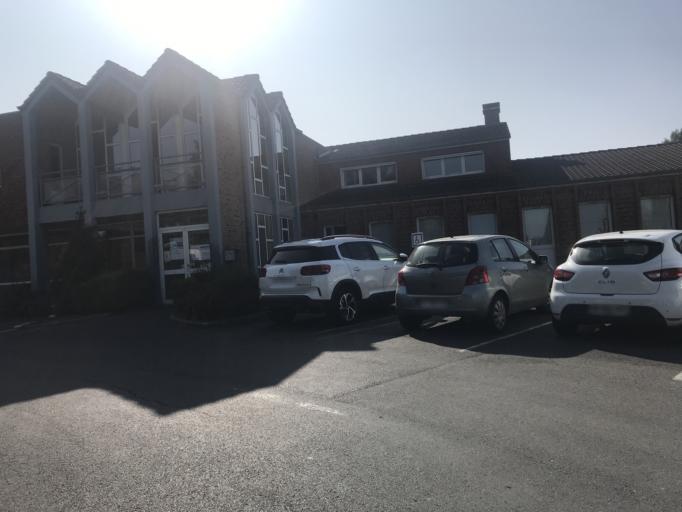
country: FR
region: Nord-Pas-de-Calais
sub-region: Departement du Pas-de-Calais
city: Billy-Montigny
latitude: 50.4207
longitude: 2.9062
